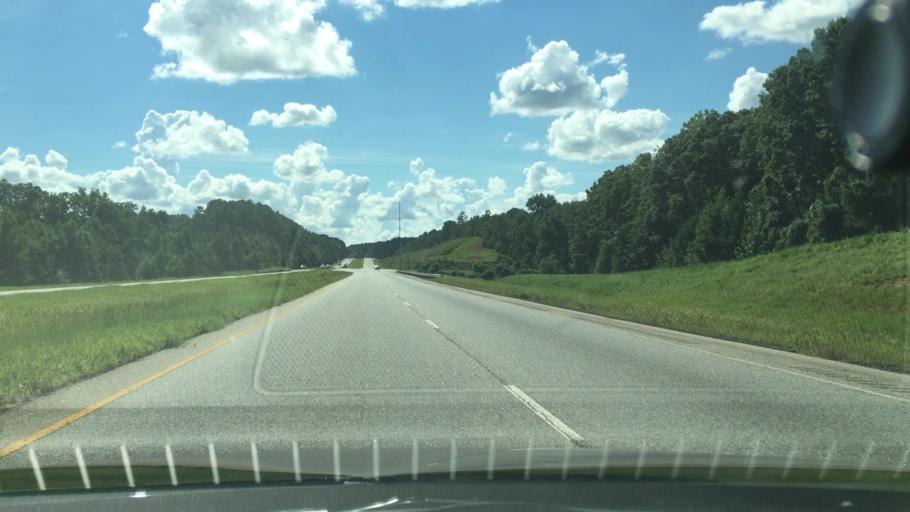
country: US
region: Georgia
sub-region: Spalding County
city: East Griffin
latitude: 33.2371
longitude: -84.1872
